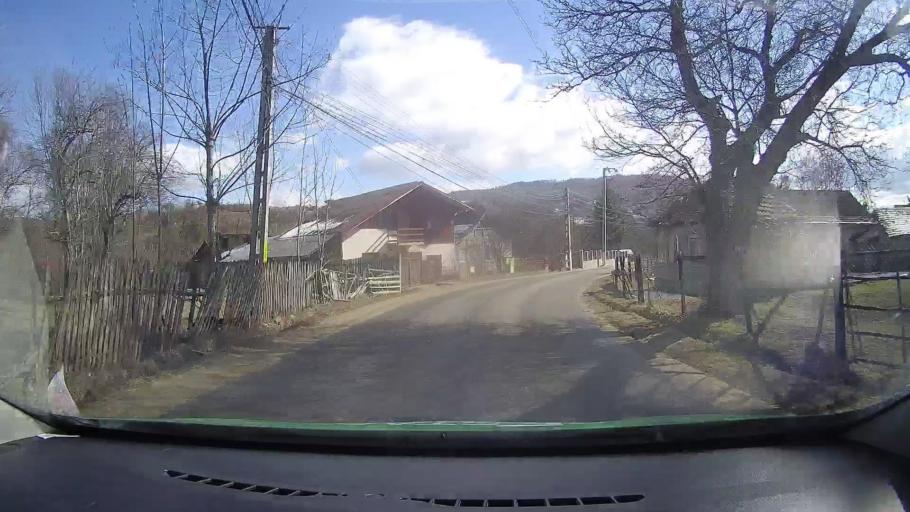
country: RO
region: Dambovita
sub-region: Comuna Runcu
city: Runcu
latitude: 45.1737
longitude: 25.3904
